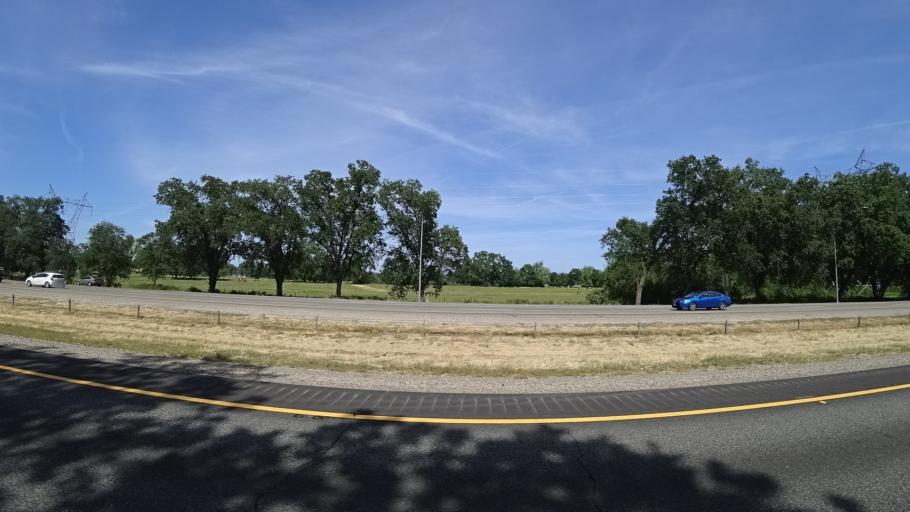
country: US
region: California
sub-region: Shasta County
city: Anderson
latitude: 40.4657
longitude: -122.3052
